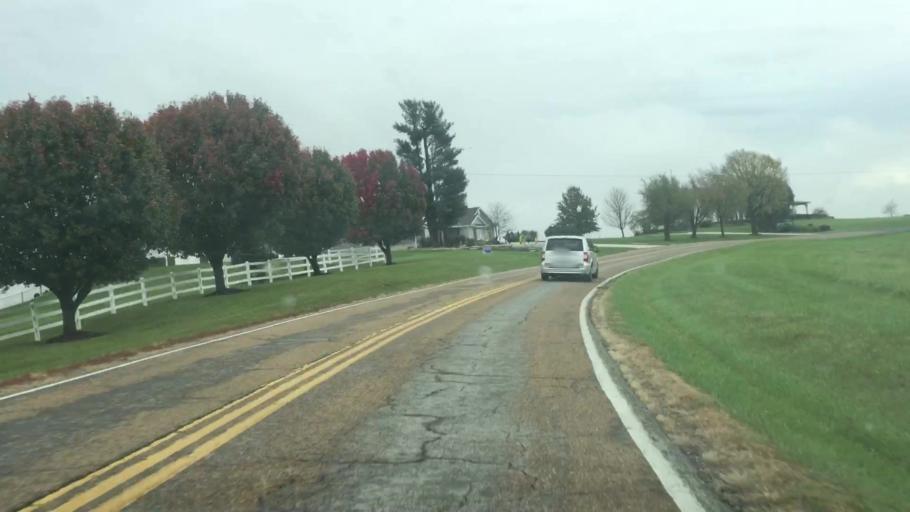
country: US
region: Missouri
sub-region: Callaway County
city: Fulton
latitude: 38.7404
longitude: -91.7060
